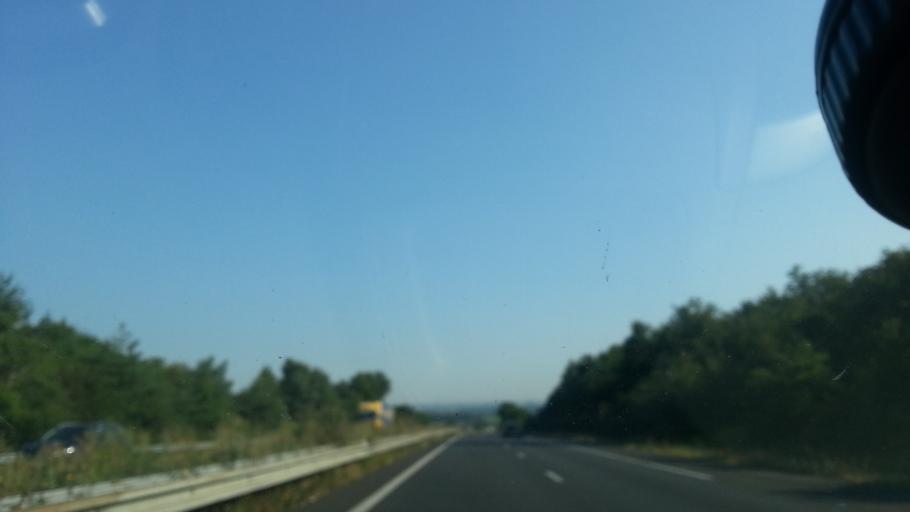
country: FR
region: Poitou-Charentes
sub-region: Departement de la Vienne
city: Les Ormes
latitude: 46.9862
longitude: 0.5482
